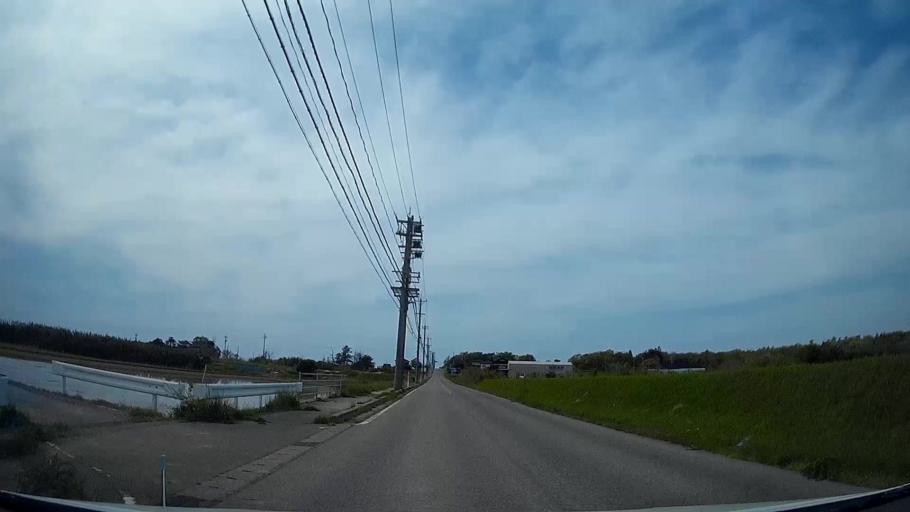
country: JP
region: Ishikawa
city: Hakui
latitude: 37.0143
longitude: 136.7555
